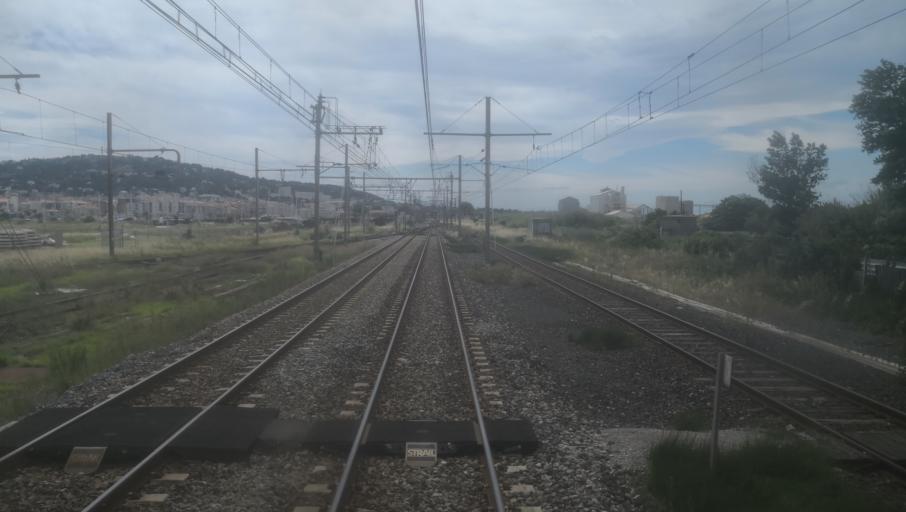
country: FR
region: Languedoc-Roussillon
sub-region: Departement de l'Herault
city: Sete
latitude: 43.4151
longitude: 3.7076
